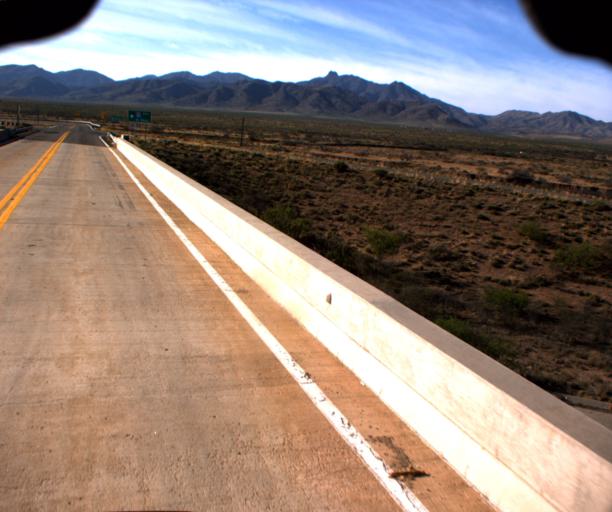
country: US
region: Arizona
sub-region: Cochise County
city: Willcox
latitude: 32.3623
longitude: -109.6209
